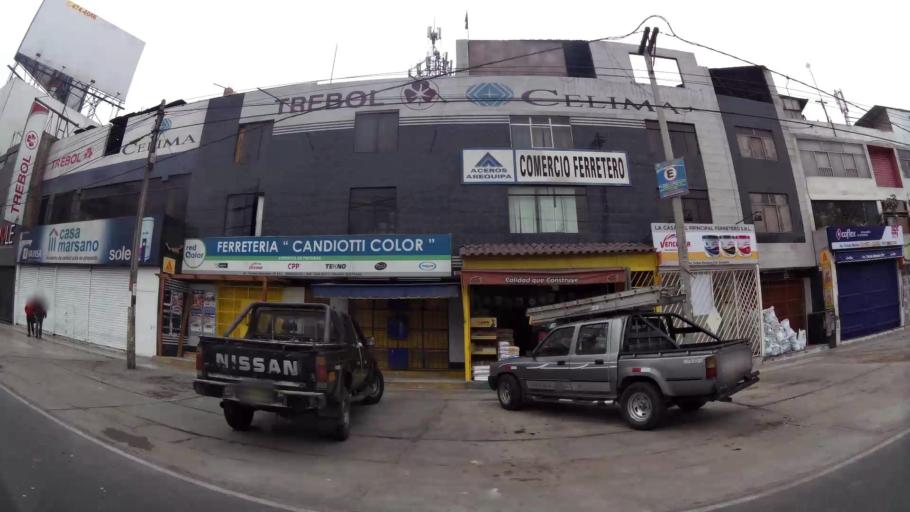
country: PE
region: Lima
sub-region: Lima
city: Surco
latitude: -12.1085
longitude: -77.0150
